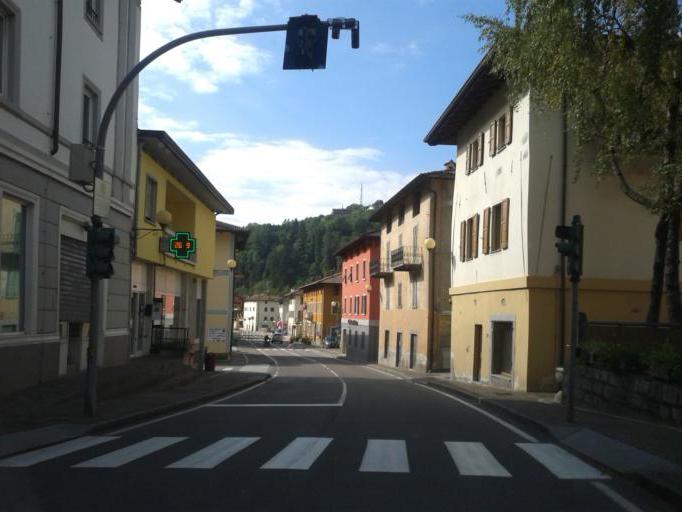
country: IT
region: Trentino-Alto Adige
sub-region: Provincia di Trento
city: Creto
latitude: 45.9398
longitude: 10.6392
